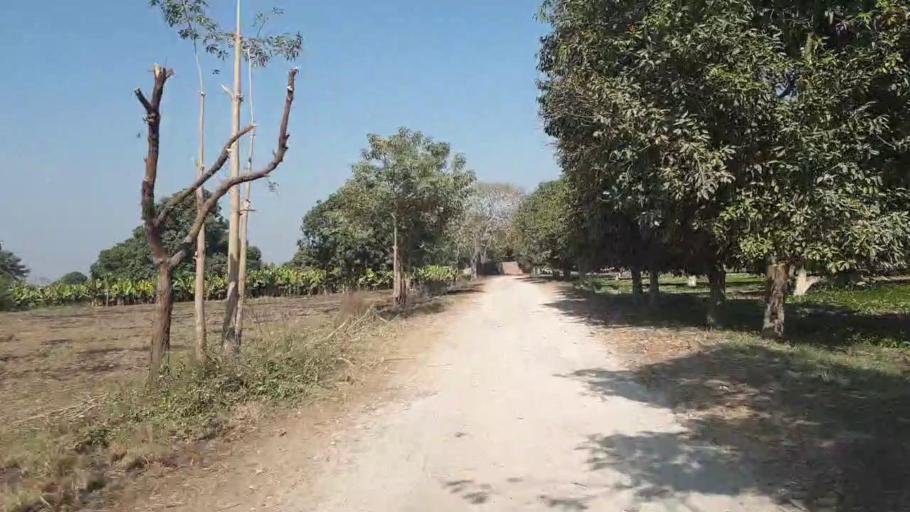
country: PK
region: Sindh
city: Chambar
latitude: 25.3589
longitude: 68.8042
